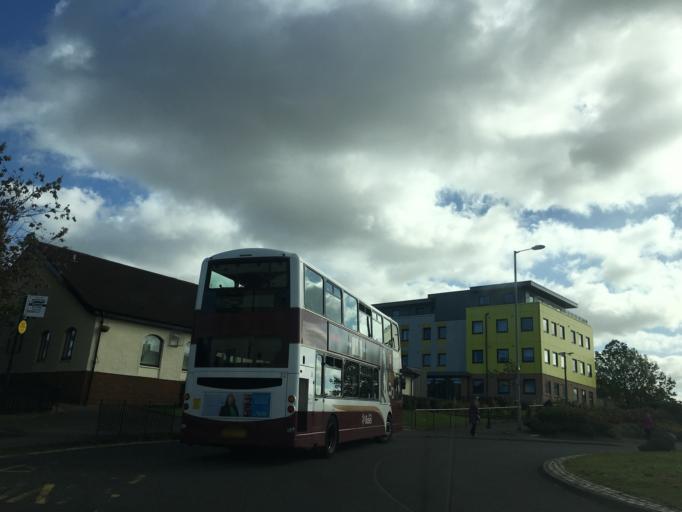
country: GB
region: Scotland
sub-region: Edinburgh
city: Currie
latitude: 55.9522
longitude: -3.3038
